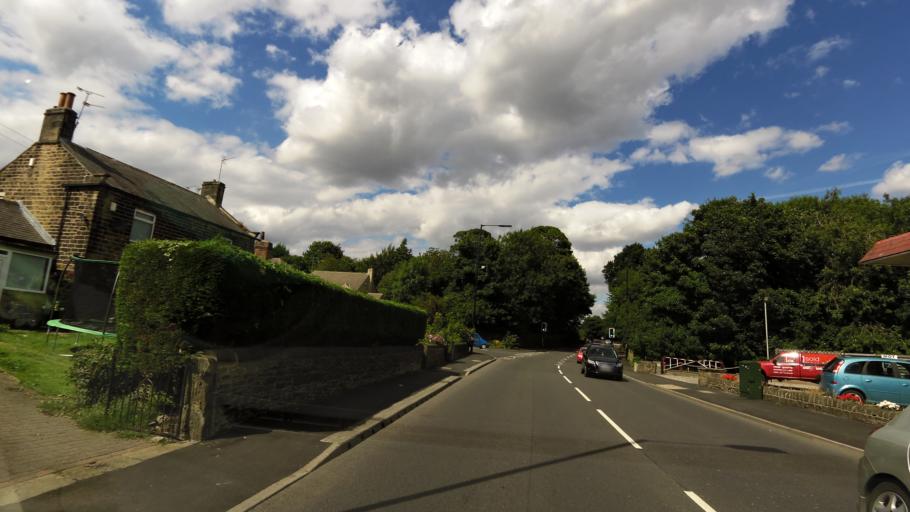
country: GB
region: England
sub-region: Sheffield
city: Chapletown
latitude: 53.4413
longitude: -1.4963
